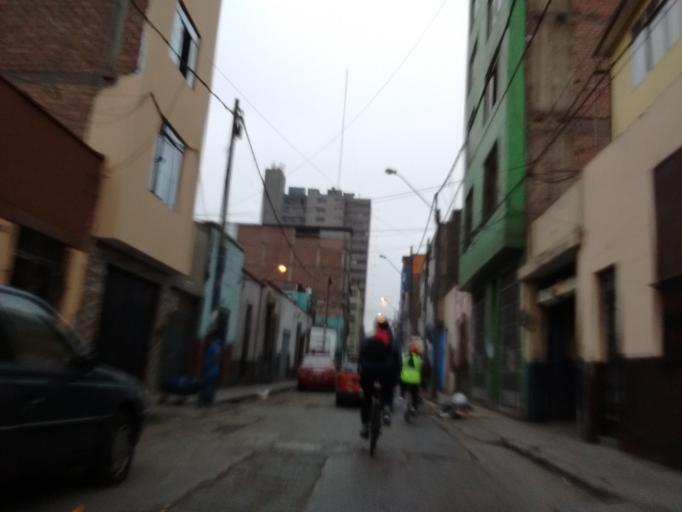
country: PE
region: Lima
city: Lima
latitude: -12.0609
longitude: -77.0288
